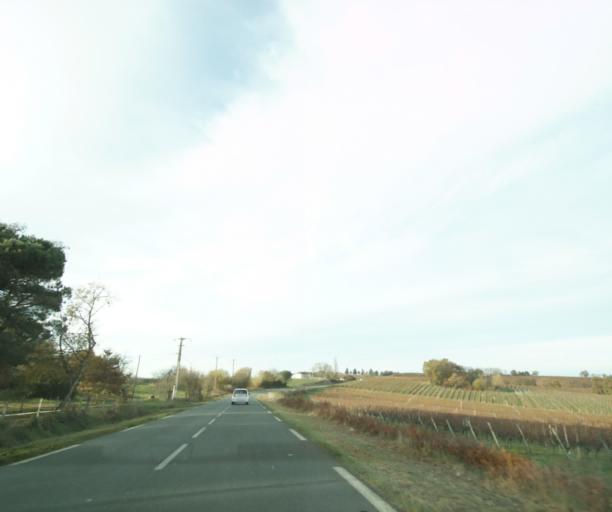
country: FR
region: Midi-Pyrenees
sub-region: Departement du Gers
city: Eauze
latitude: 43.8052
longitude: 0.0974
